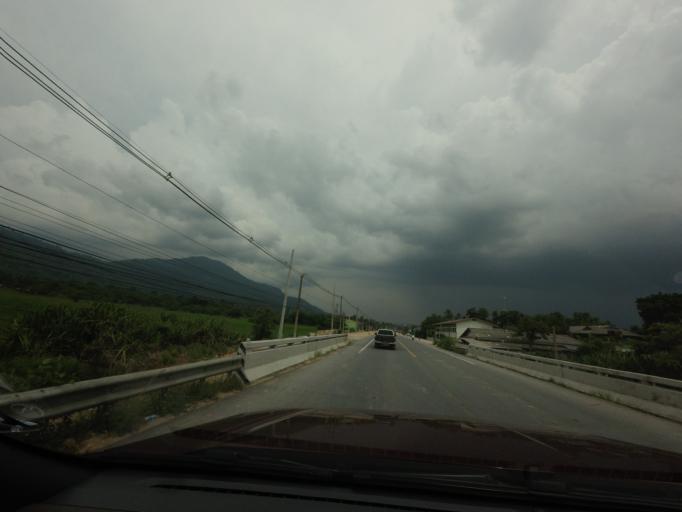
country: TH
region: Yala
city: Krong Pi Nang
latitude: 6.4472
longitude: 101.2765
